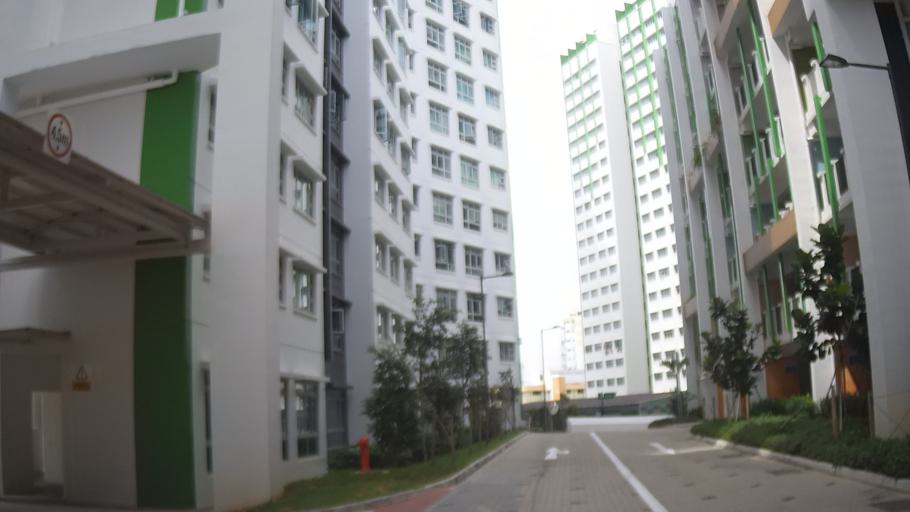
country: MY
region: Johor
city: Johor Bahru
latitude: 1.4361
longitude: 103.7766
